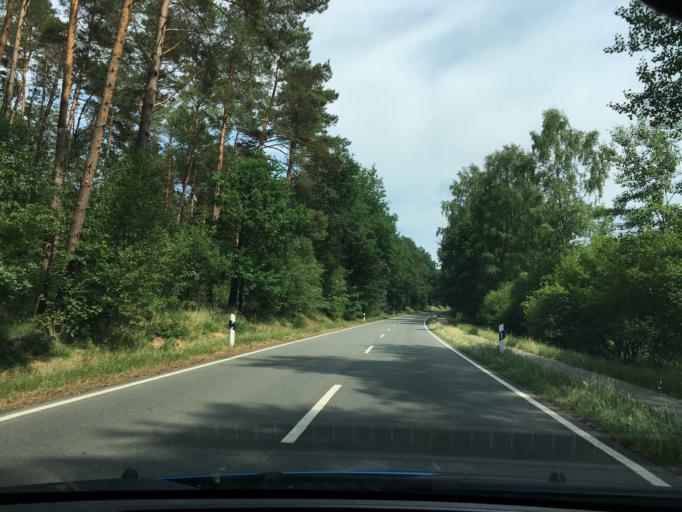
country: DE
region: Lower Saxony
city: Jesteburg
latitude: 53.2709
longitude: 9.9462
